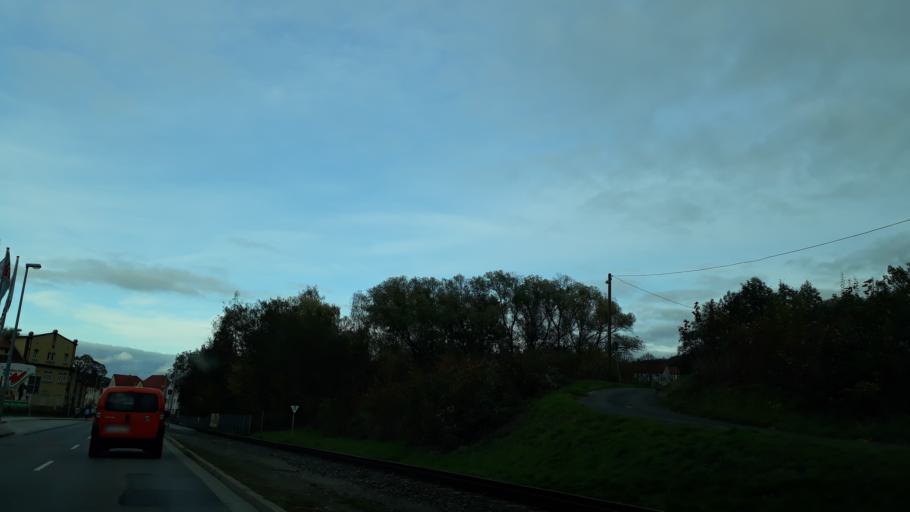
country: DE
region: Saxony
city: Rabenau
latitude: 50.9758
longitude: 13.6237
